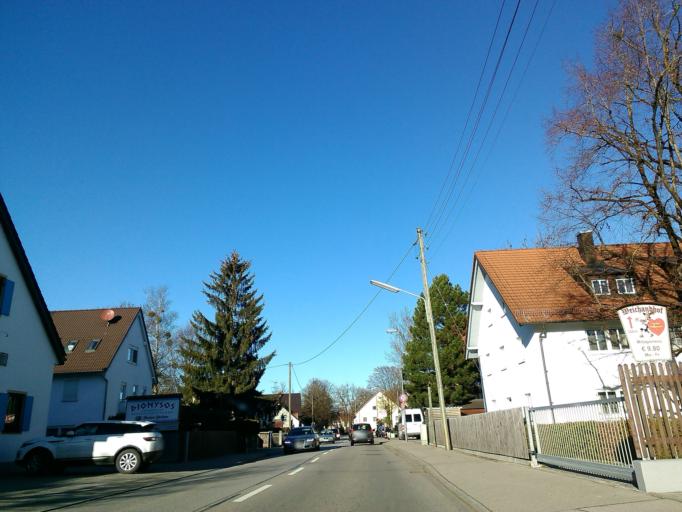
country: DE
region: Bavaria
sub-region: Upper Bavaria
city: Pasing
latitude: 48.1663
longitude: 11.4573
